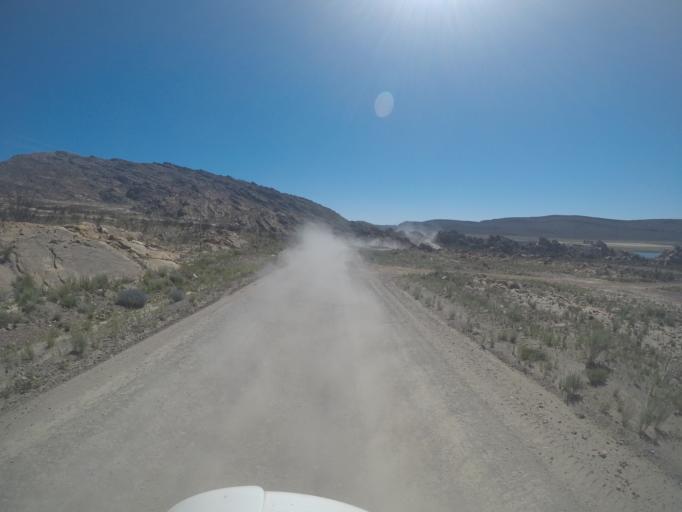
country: ZA
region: Western Cape
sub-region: Cape Winelands District Municipality
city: Ceres
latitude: -32.8493
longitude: 19.4456
